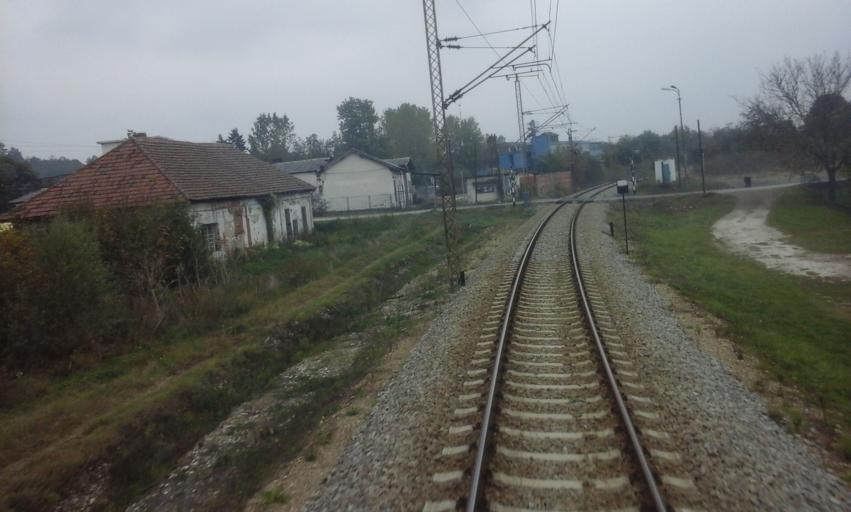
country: RS
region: Central Serbia
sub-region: Belgrade
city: Mladenovac
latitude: 44.4765
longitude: 20.6633
